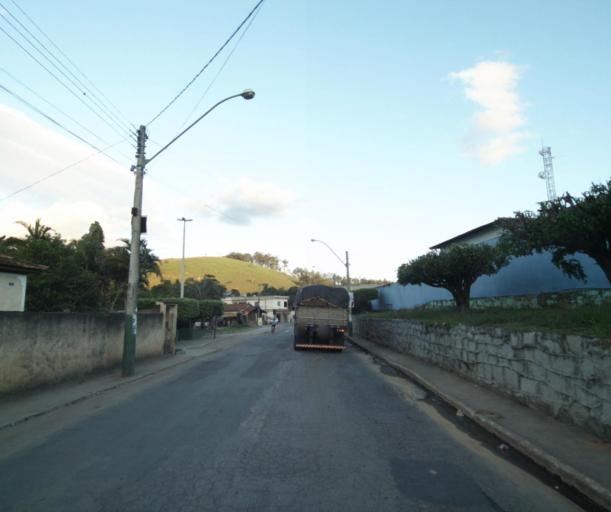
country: BR
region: Rio de Janeiro
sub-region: Bom Jesus Do Itabapoana
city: Bom Jesus do Itabapoana
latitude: -21.1509
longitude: -41.5695
